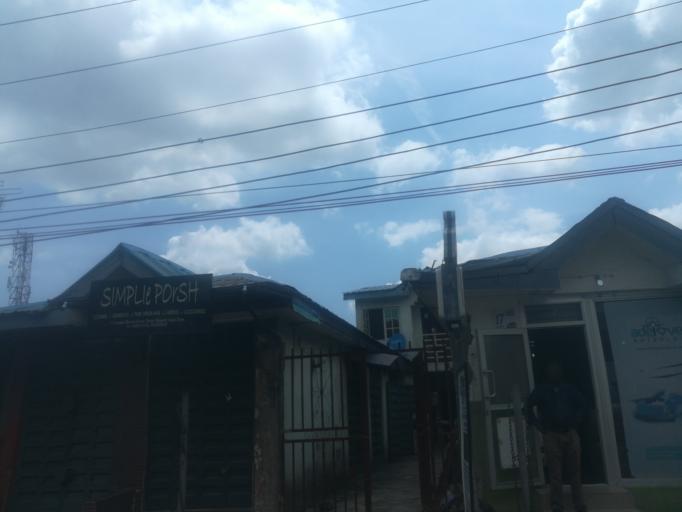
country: NG
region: Lagos
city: Somolu
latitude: 6.5571
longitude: 3.3867
